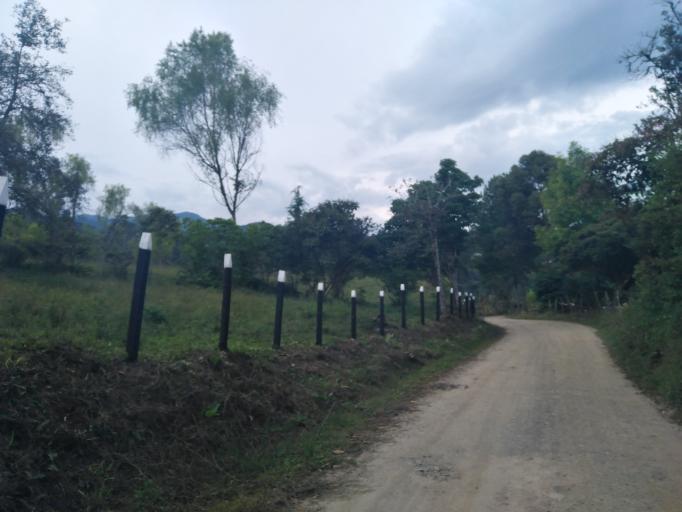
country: CO
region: Cundinamarca
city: Tenza
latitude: 5.1056
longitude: -73.4152
